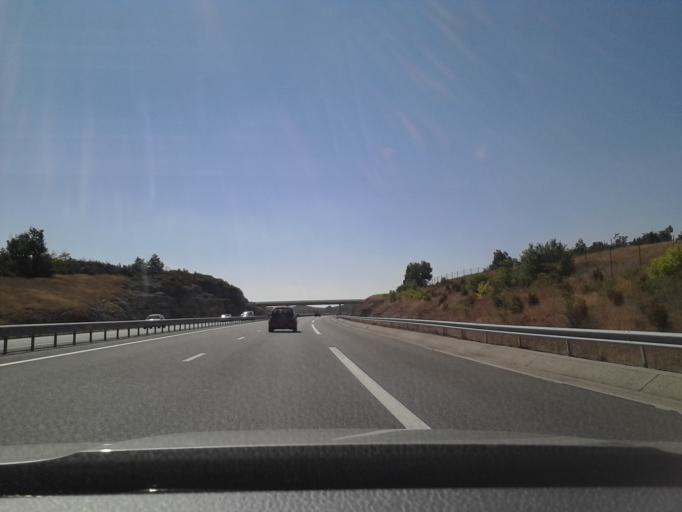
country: FR
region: Midi-Pyrenees
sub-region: Departement de l'Aveyron
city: Creissels
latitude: 44.0542
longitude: 3.0433
